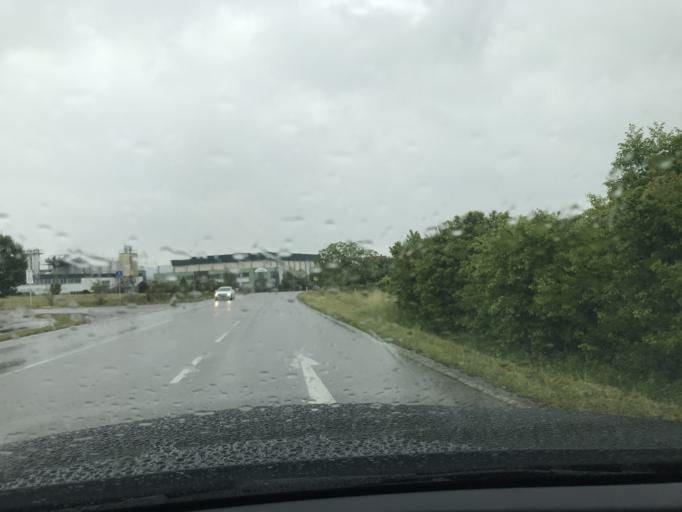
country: DE
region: Baden-Wuerttemberg
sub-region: Regierungsbezirk Stuttgart
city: Leutenbach
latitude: 48.8817
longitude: 9.3873
